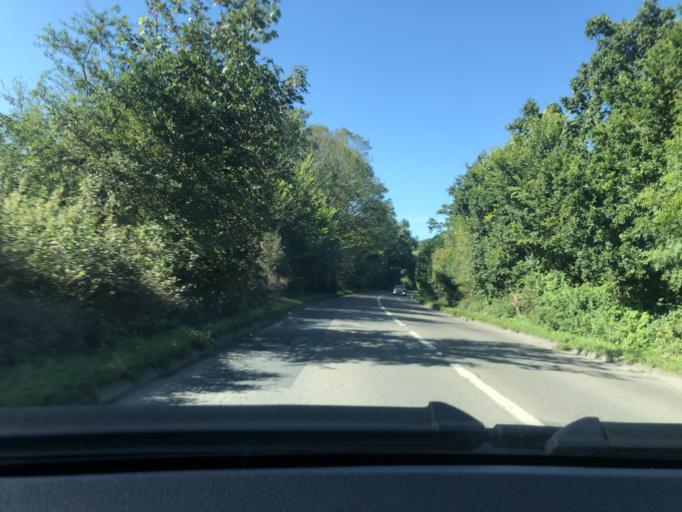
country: GB
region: England
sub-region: Somerset
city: Puriton
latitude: 51.1568
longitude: -2.9606
